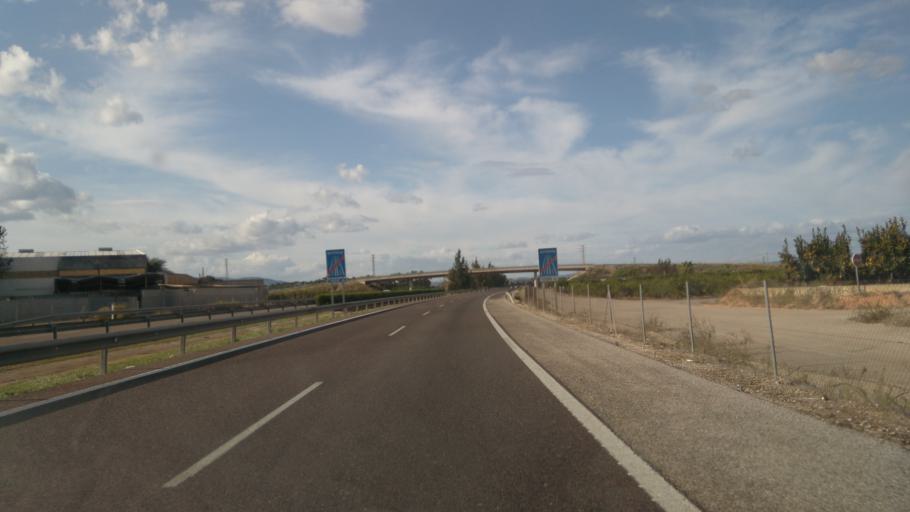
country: ES
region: Valencia
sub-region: Provincia de Valencia
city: Guadassuar
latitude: 39.1811
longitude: -0.4862
